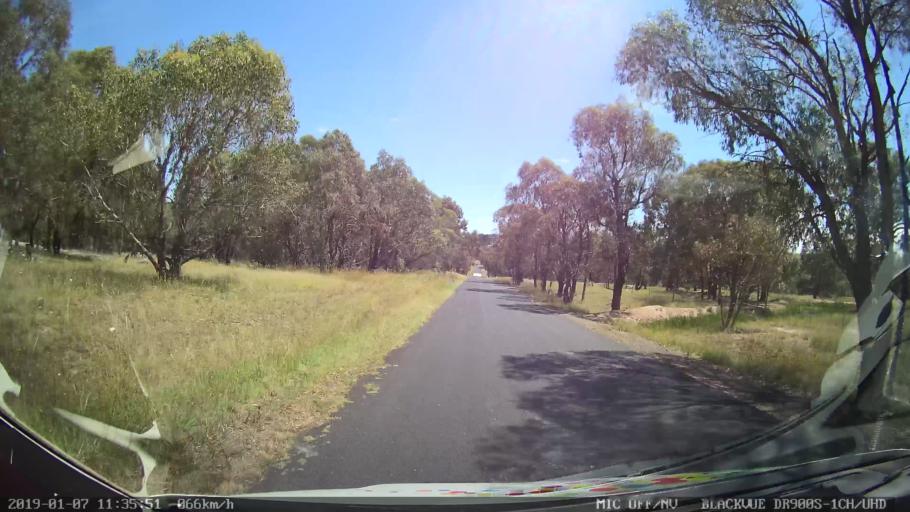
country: AU
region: New South Wales
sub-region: Armidale Dumaresq
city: Armidale
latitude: -30.3758
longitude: 151.5585
